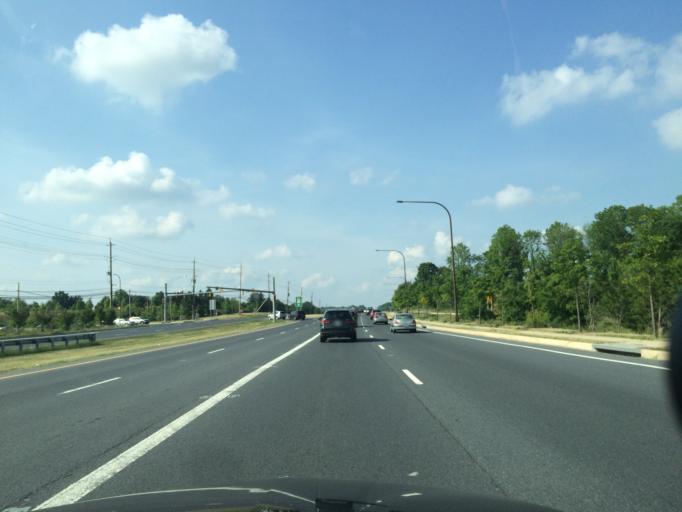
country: US
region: Maryland
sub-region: Montgomery County
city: Rossmoor
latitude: 39.1188
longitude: -77.0746
